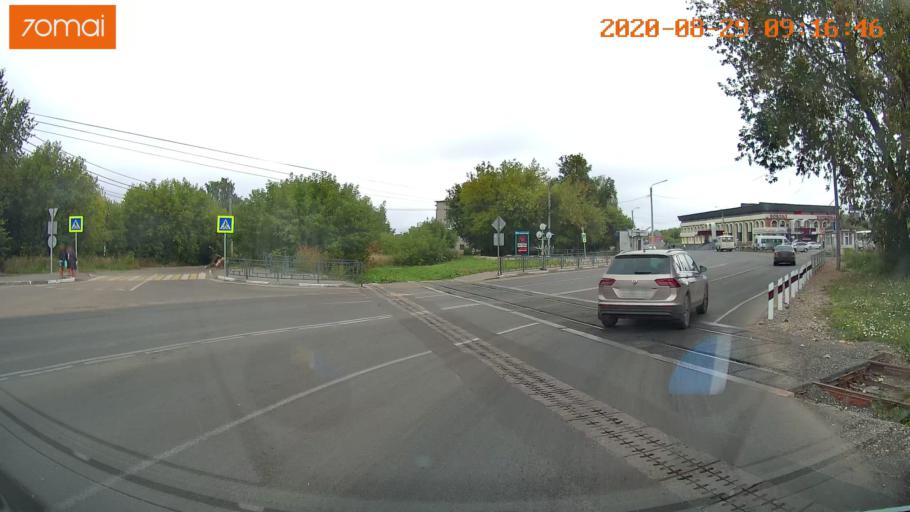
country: RU
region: Ivanovo
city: Kineshma
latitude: 57.4418
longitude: 42.1419
